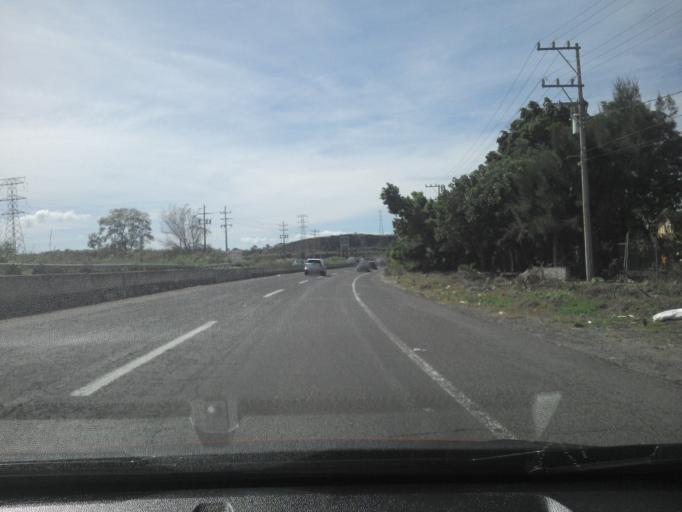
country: MX
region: Jalisco
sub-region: Tala
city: Los Ruisenores
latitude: 20.6824
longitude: -103.6953
